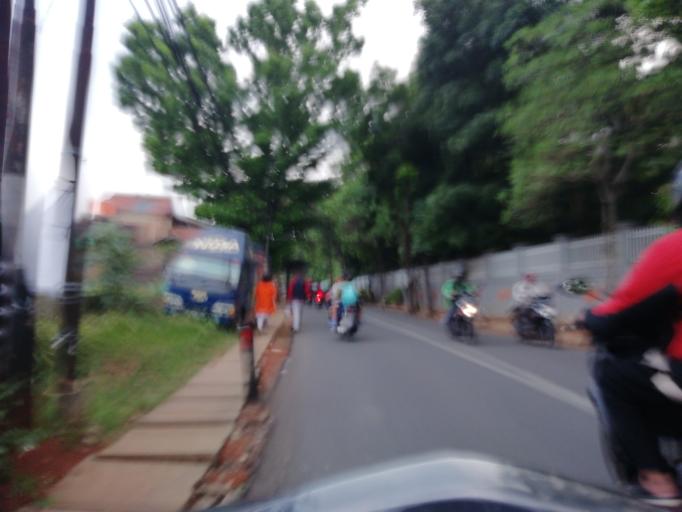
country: ID
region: West Java
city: Depok
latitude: -6.3379
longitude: 106.8290
